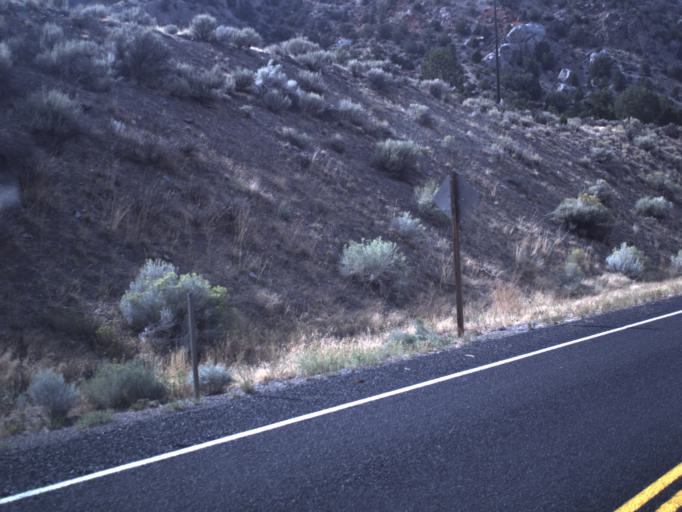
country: US
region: Utah
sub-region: Sevier County
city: Monroe
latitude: 38.5533
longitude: -112.2706
